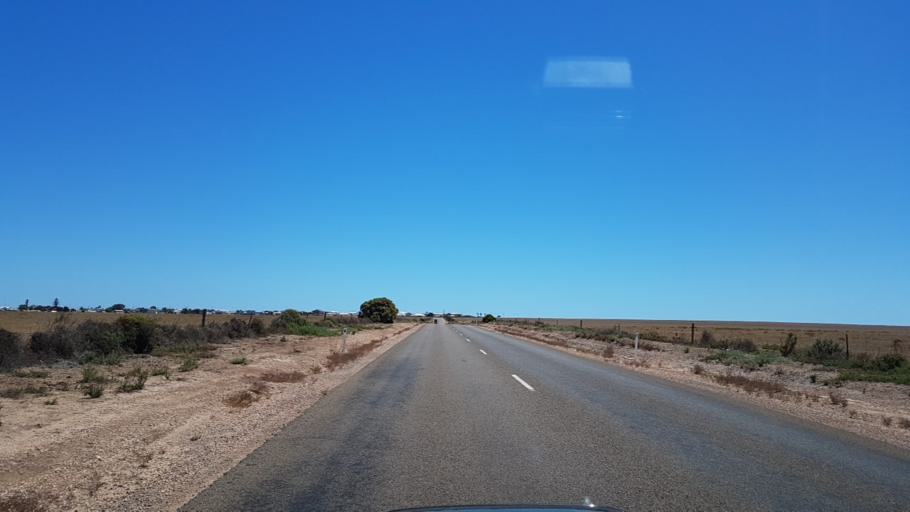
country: AU
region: South Australia
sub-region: Copper Coast
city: Wallaroo
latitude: -33.9043
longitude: 137.6388
